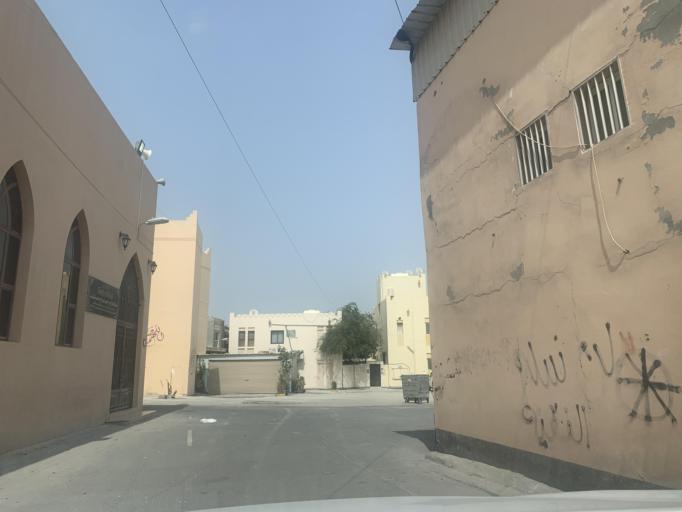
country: BH
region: Manama
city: Jidd Hafs
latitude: 26.2196
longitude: 50.4662
